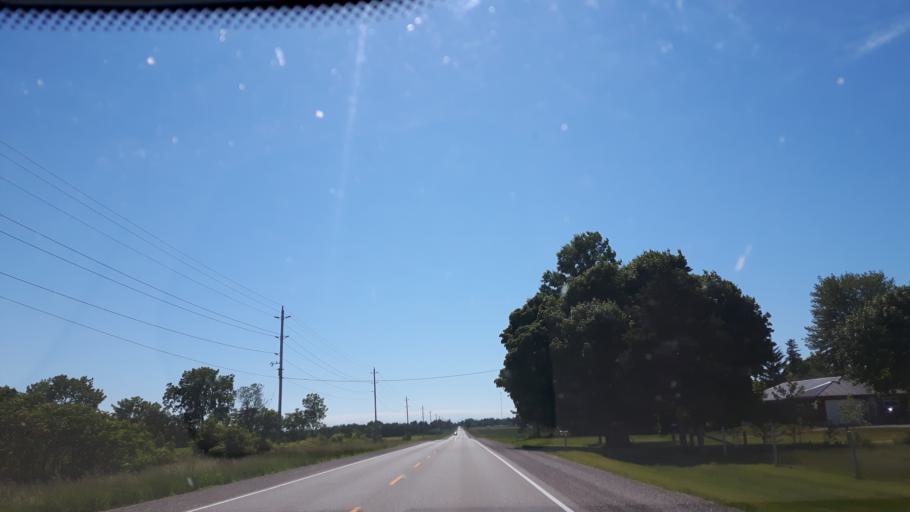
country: CA
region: Ontario
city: Bluewater
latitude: 43.4181
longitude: -81.6544
